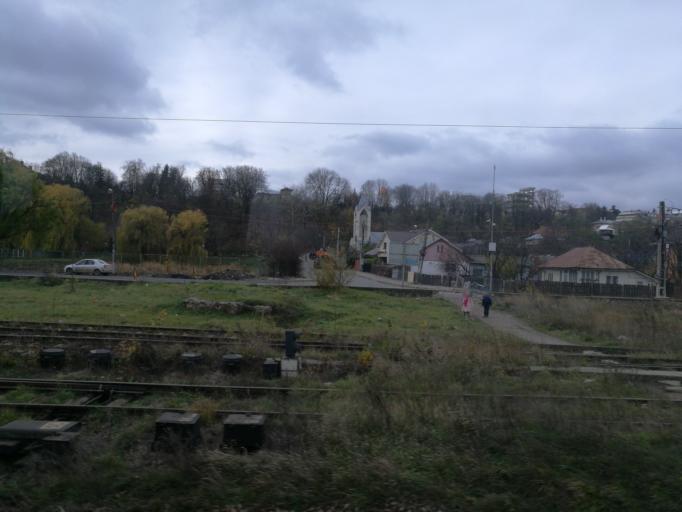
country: RO
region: Iasi
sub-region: Municipiul Pascani
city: Pascani
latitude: 47.2472
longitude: 26.7299
